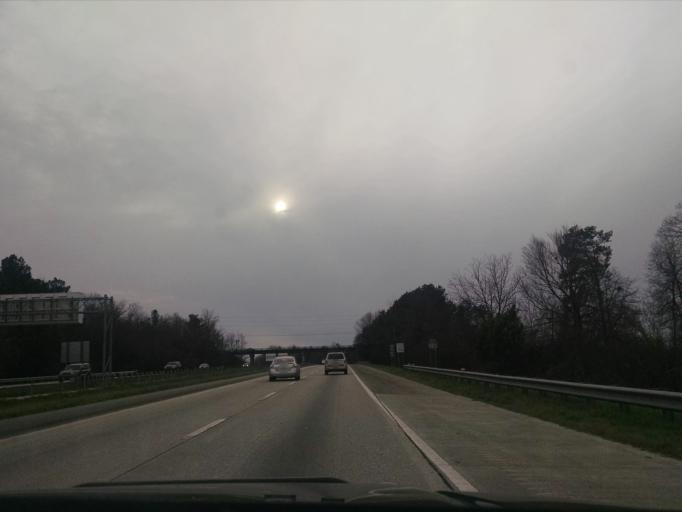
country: US
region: Georgia
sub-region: Hall County
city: Oakwood
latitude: 34.2172
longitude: -83.8787
